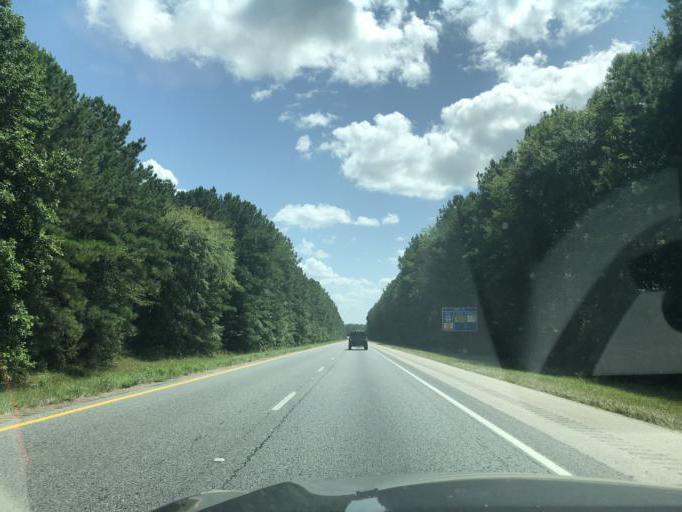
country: US
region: Georgia
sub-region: Troup County
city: La Grange
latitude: 32.9827
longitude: -84.9514
